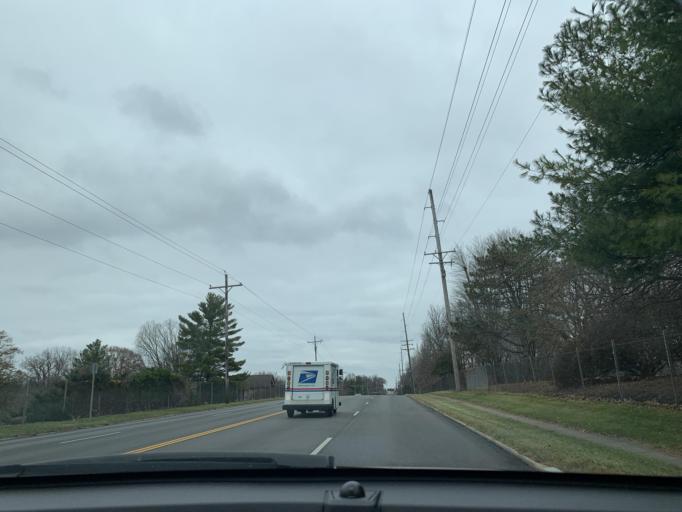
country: US
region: Illinois
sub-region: Sangamon County
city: Leland Grove
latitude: 39.7840
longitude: -89.6870
